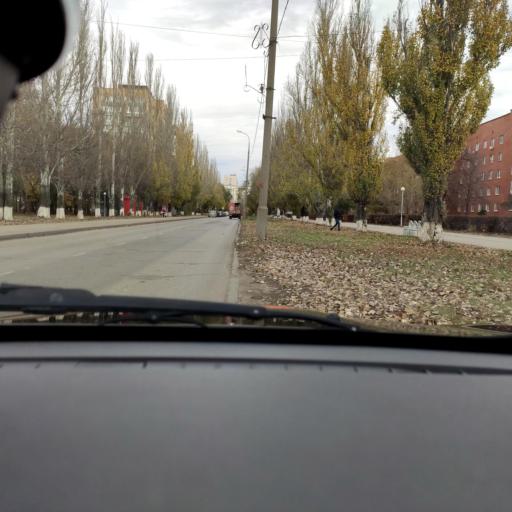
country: RU
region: Samara
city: Tol'yatti
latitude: 53.5325
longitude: 49.2669
